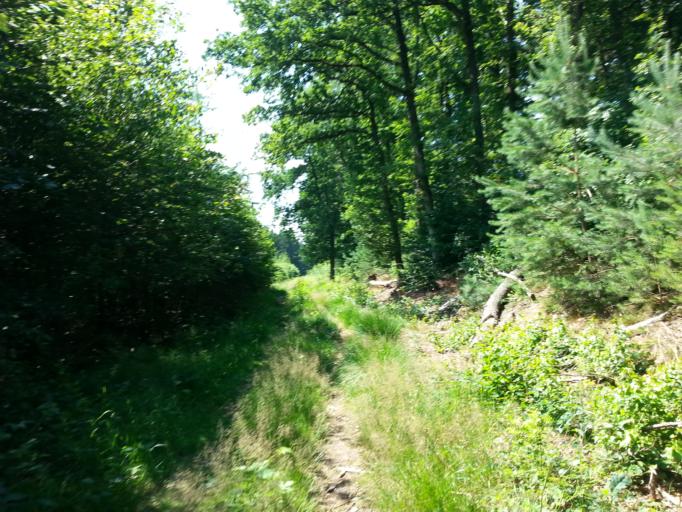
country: NL
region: Utrecht
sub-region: Gemeente Woudenberg
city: Woudenberg
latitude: 52.1010
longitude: 5.3894
